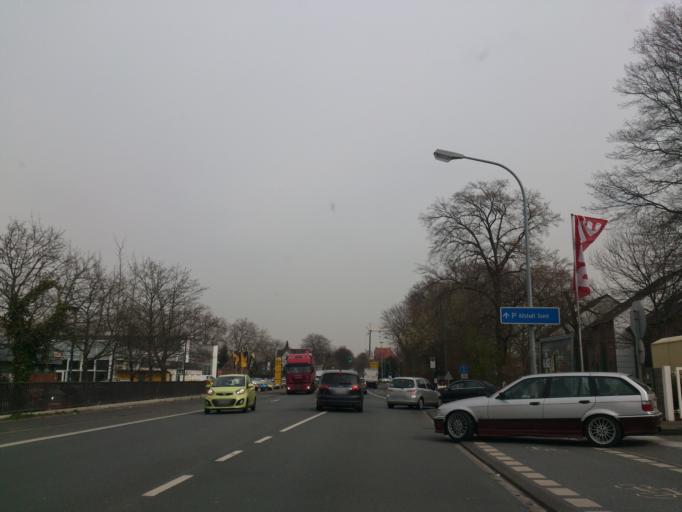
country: DE
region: North Rhine-Westphalia
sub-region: Regierungsbezirk Arnsberg
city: Soest
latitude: 51.5653
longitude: 8.0916
